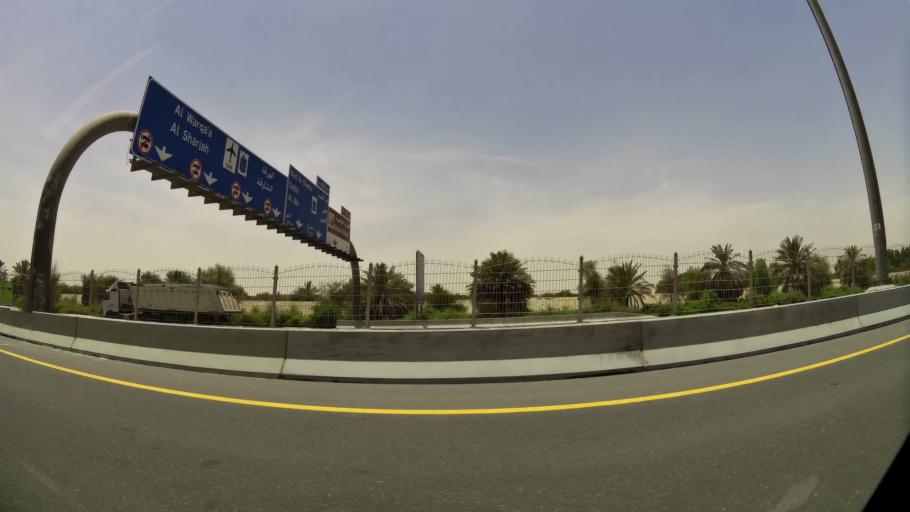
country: AE
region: Dubai
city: Dubai
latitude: 25.0607
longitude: 55.2870
